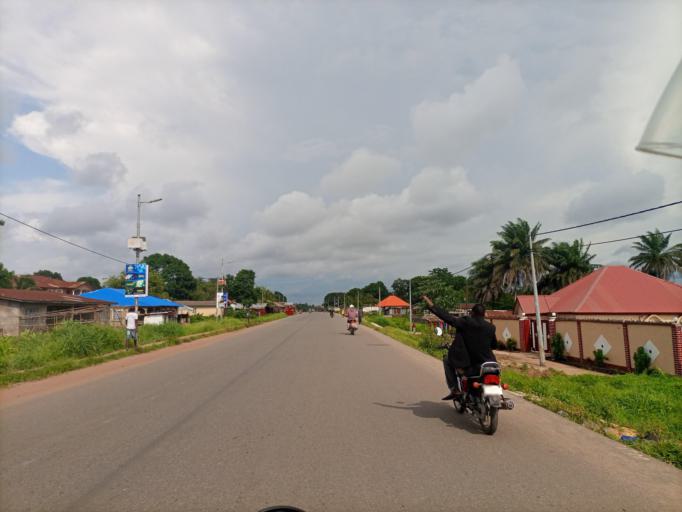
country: SL
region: Northern Province
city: Masoyila
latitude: 8.6013
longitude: -13.1767
